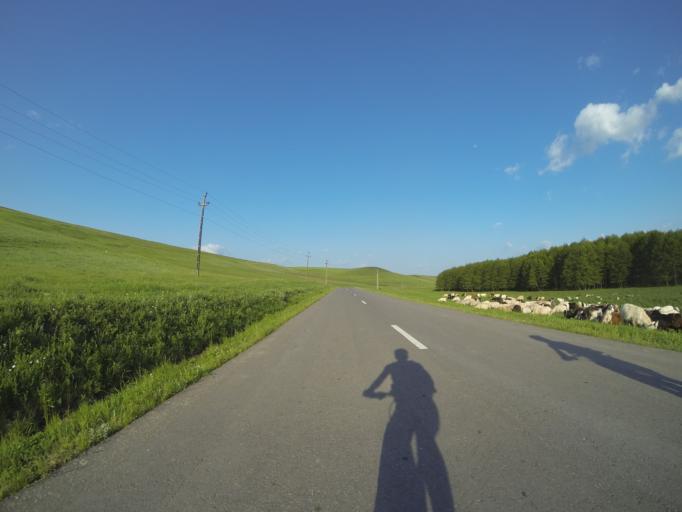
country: RO
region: Dolj
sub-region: Comuna Vela
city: Vela
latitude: 44.2725
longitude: 23.3549
